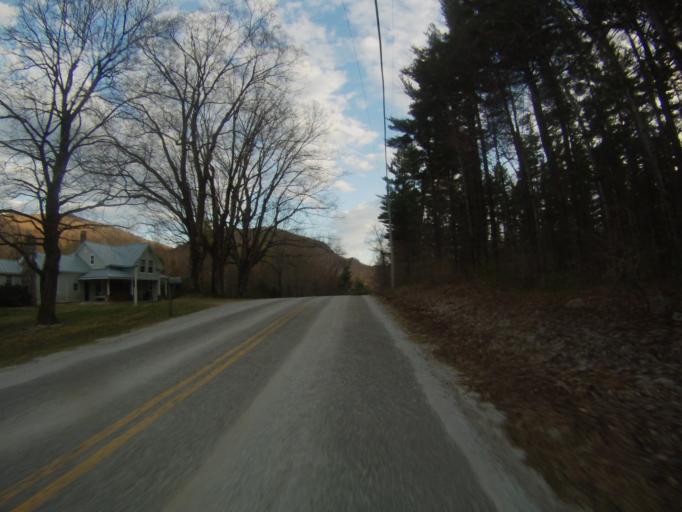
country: US
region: Vermont
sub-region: Rutland County
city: Brandon
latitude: 43.8439
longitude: -72.9958
